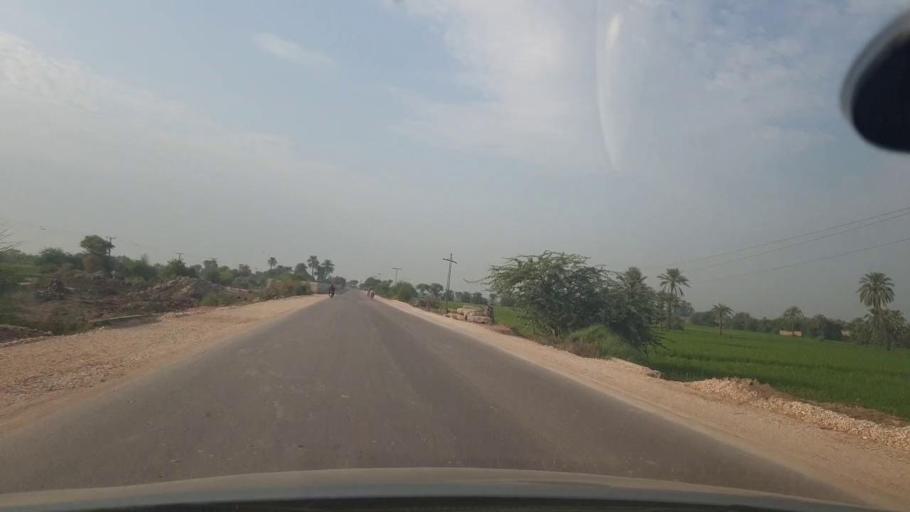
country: PK
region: Sindh
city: Jacobabad
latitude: 28.1960
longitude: 68.3677
